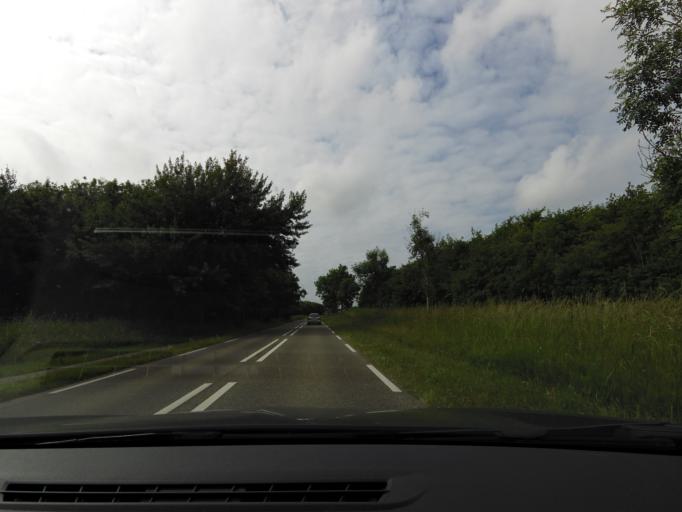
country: NL
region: Zeeland
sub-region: Gemeente Vlissingen
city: Vlissingen
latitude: 51.5240
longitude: 3.4506
